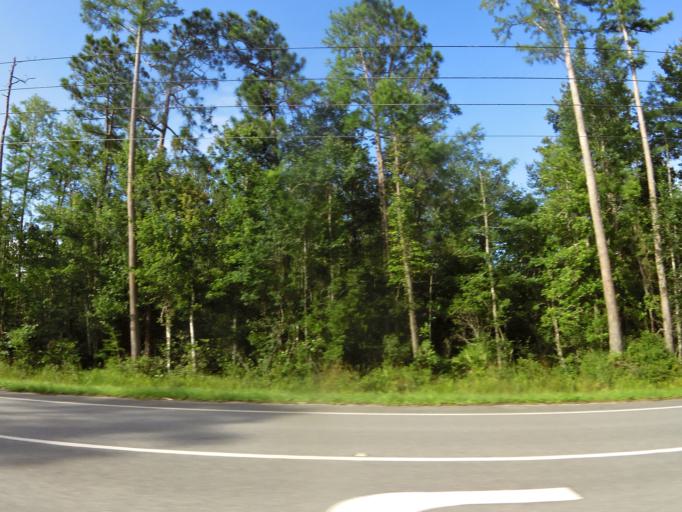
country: US
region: Florida
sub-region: Clay County
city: Green Cove Springs
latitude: 30.0023
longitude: -81.5464
